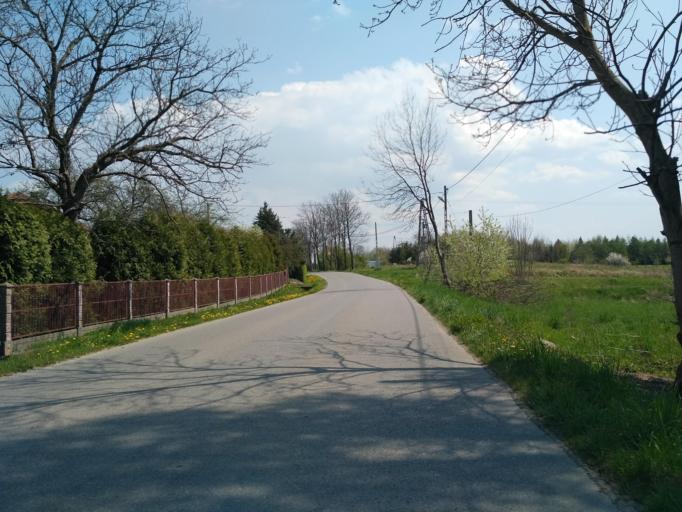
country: PL
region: Subcarpathian Voivodeship
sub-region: Powiat jasielski
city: Tarnowiec
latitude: 49.7443
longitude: 21.5727
